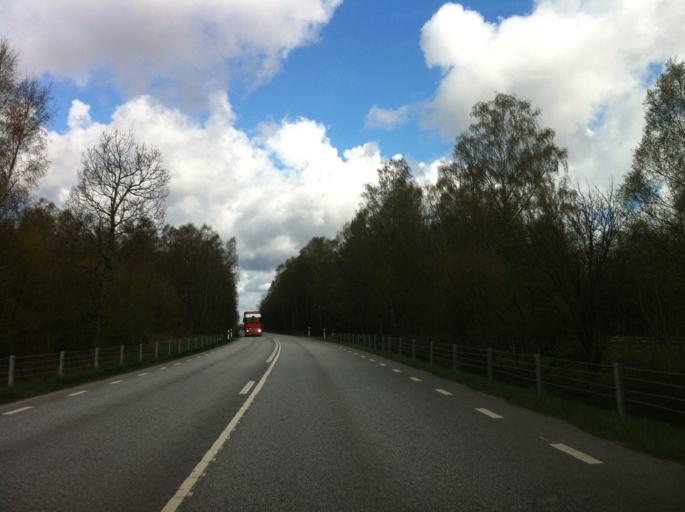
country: SE
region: Skane
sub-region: Horby Kommun
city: Hoerby
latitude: 55.8865
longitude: 13.6295
